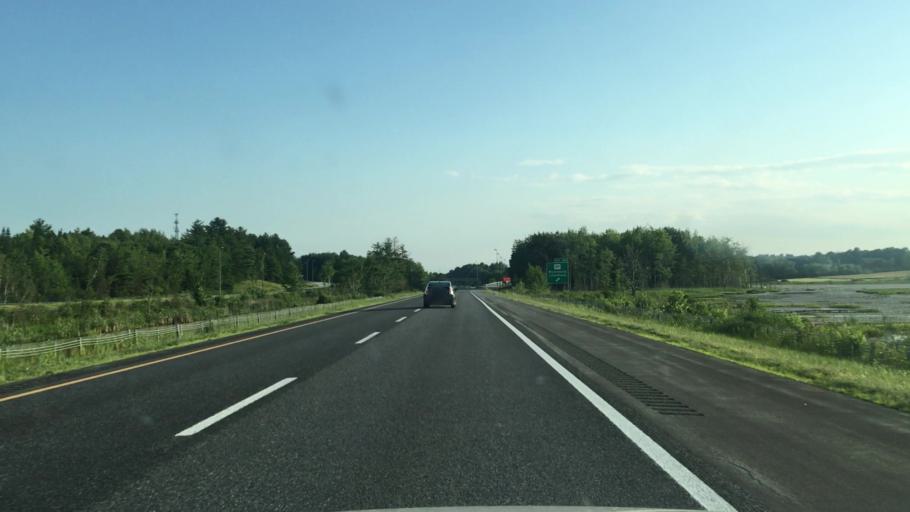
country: US
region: Maine
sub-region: Sagadahoc County
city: Richmond
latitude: 44.1062
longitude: -69.8648
